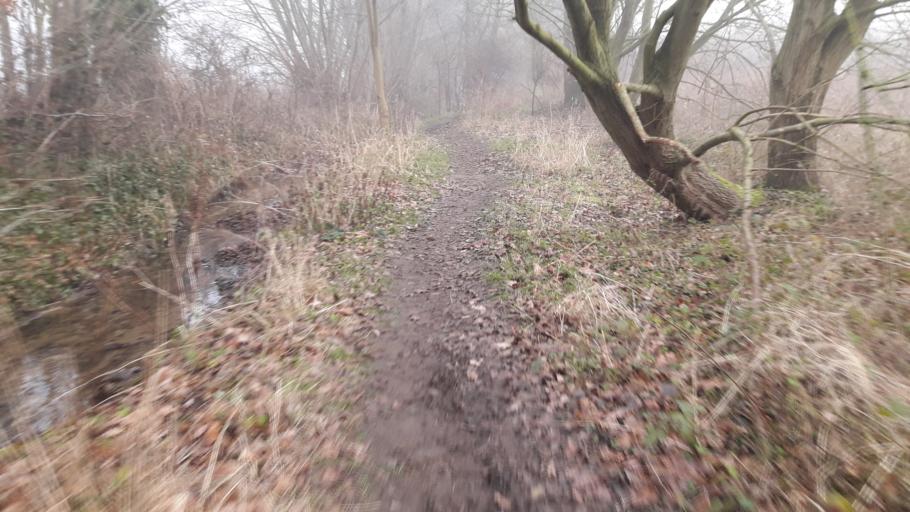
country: DE
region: Schleswig-Holstein
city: Quickborn
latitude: 53.7178
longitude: 9.8883
